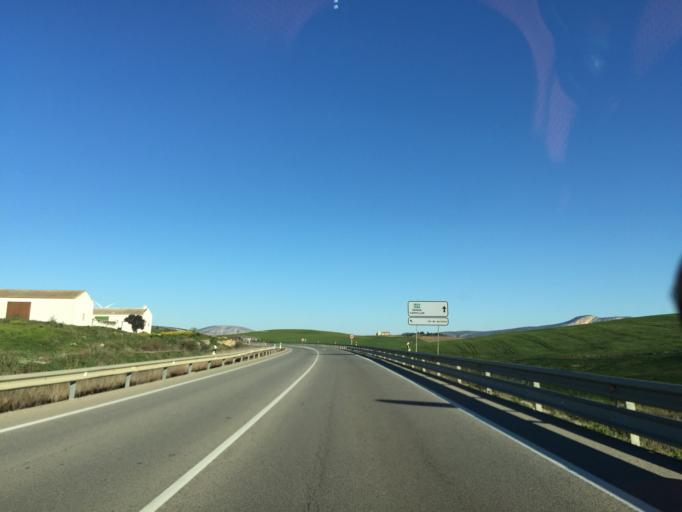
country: ES
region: Andalusia
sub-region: Provincia de Malaga
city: Ardales
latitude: 36.9201
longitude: -4.8433
